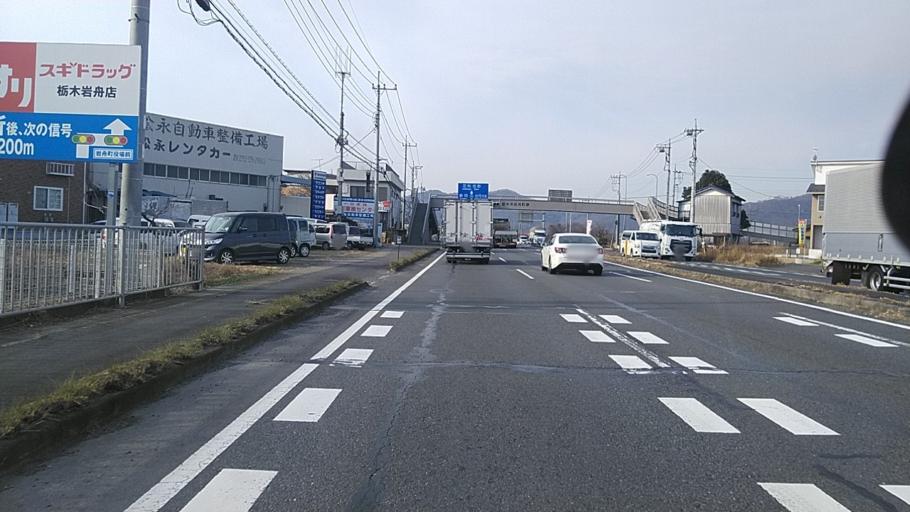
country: JP
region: Tochigi
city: Fujioka
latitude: 36.3133
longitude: 139.6561
